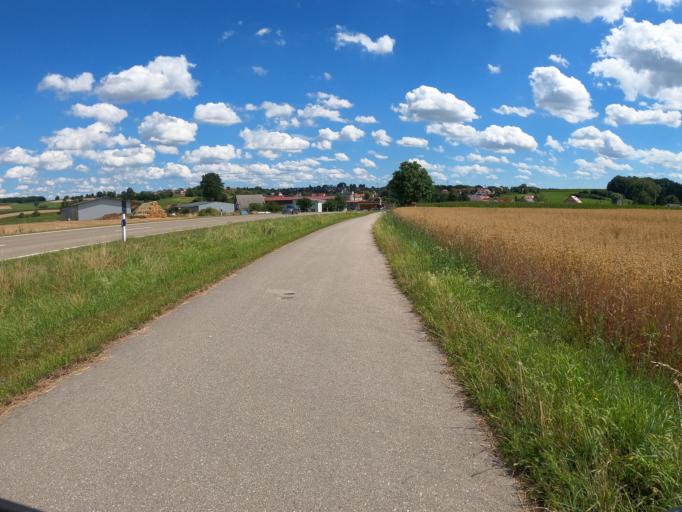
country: DE
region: Bavaria
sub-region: Swabia
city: Pfaffenhofen an der Roth
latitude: 48.4016
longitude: 10.1789
